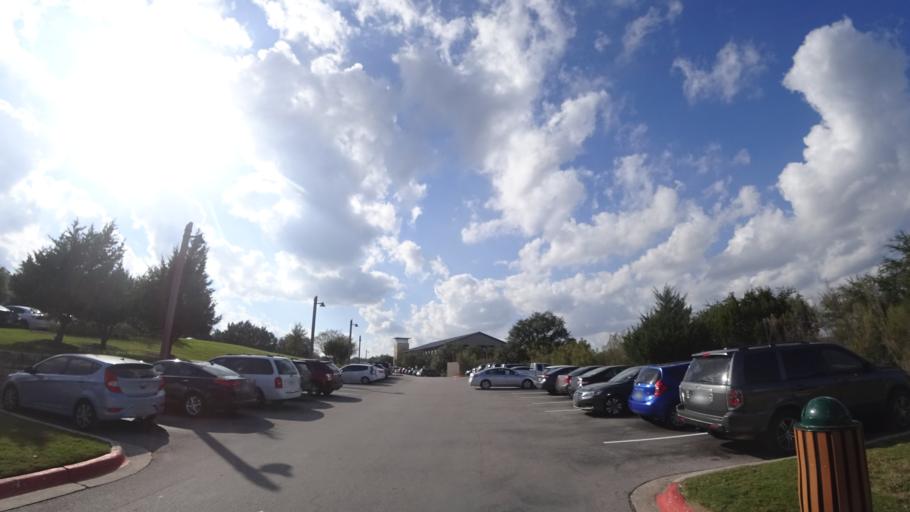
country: US
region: Texas
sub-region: Travis County
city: Barton Creek
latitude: 30.2896
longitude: -97.8700
